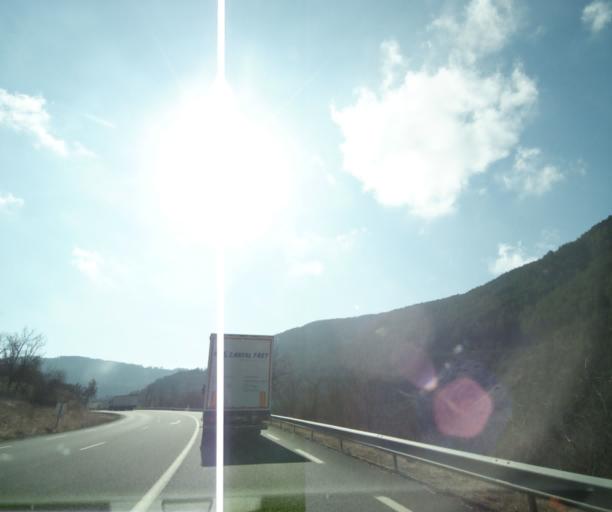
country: FR
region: Languedoc-Roussillon
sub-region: Departement de la Lozere
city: Chanac
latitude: 44.4887
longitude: 3.4184
